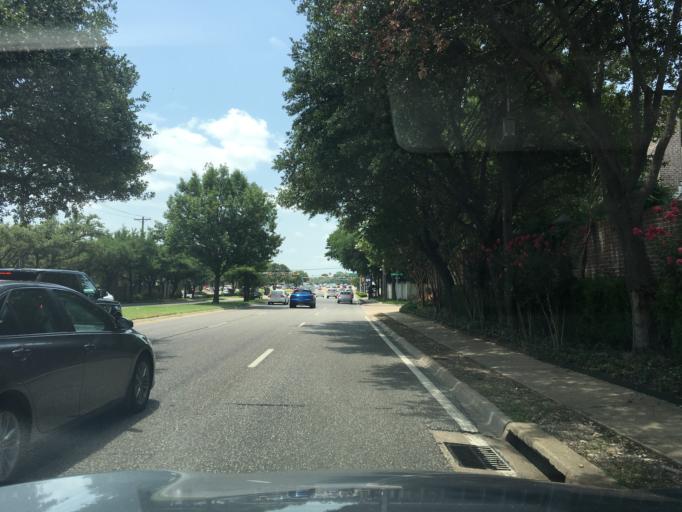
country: US
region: Texas
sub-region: Dallas County
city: Addison
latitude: 32.9127
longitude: -96.8038
